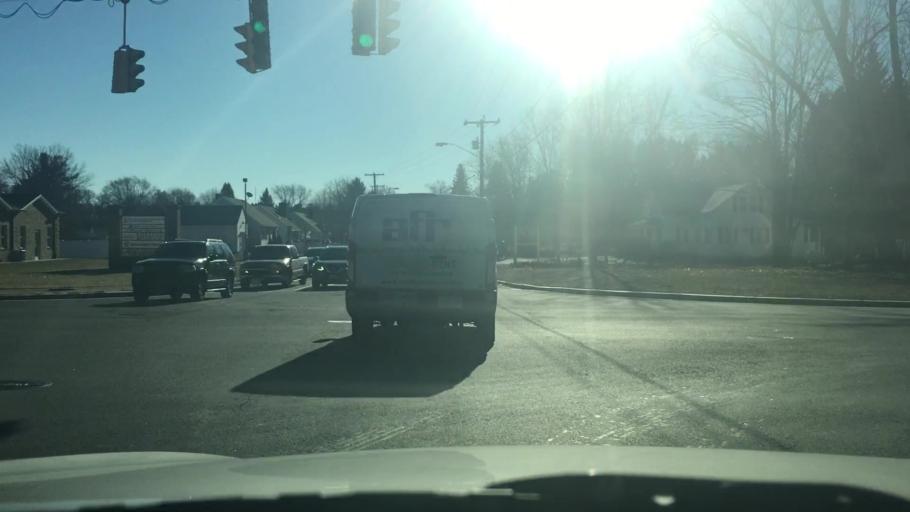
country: US
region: Massachusetts
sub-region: Hampden County
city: Ludlow
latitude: 42.1821
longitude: -72.5055
